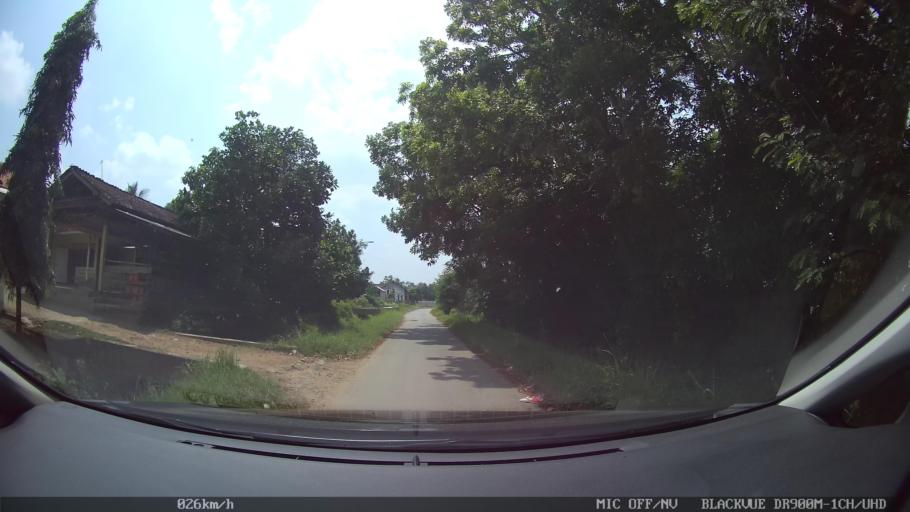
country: ID
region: Lampung
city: Pringsewu
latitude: -5.3395
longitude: 104.9761
